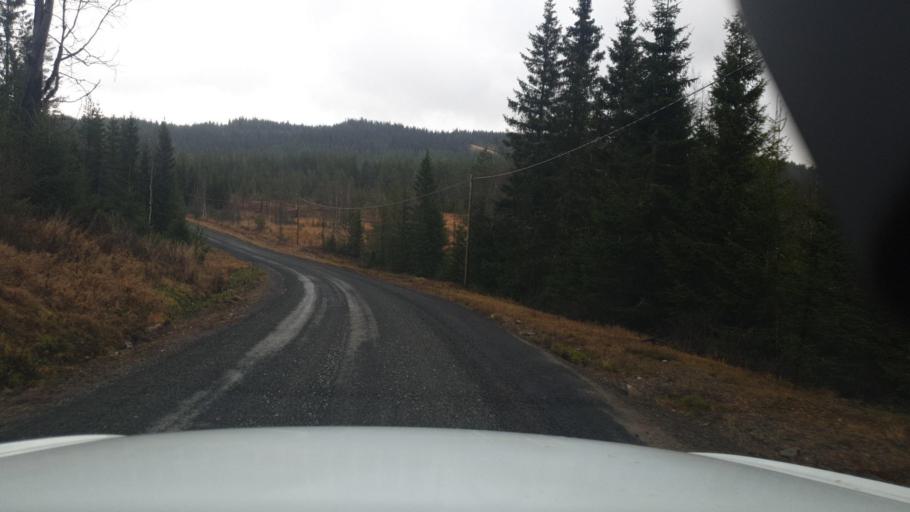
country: SE
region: Vaermland
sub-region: Torsby Kommun
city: Torsby
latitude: 60.1616
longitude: 12.6125
